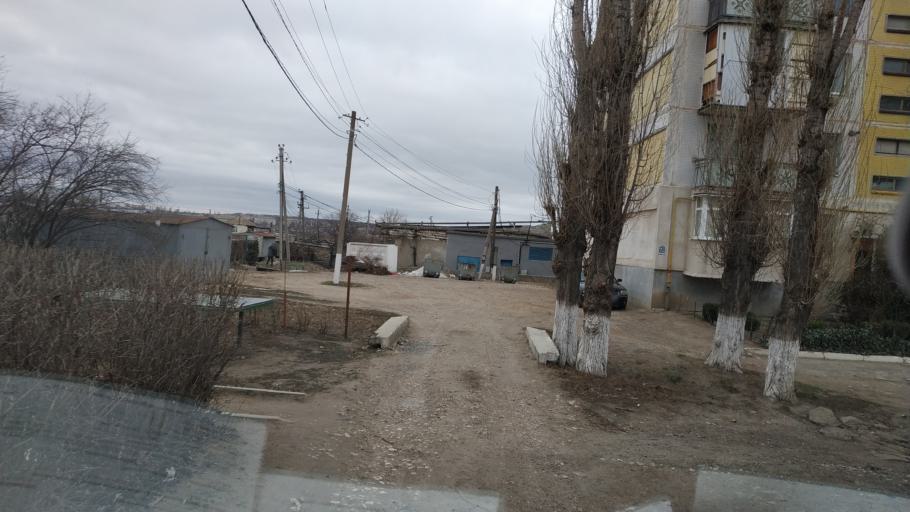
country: MD
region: Causeni
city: Causeni
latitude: 46.6463
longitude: 29.4231
